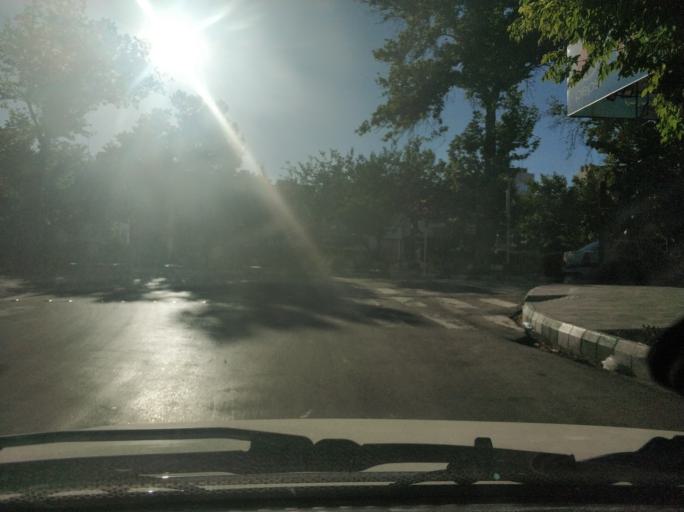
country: IR
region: Razavi Khorasan
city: Mashhad
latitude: 36.2765
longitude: 59.5933
